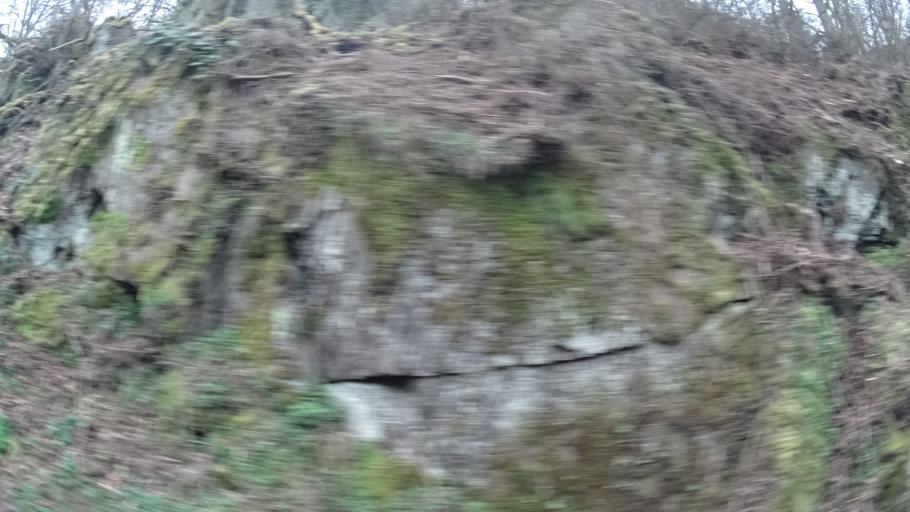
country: DE
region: Rheinland-Pfalz
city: Langenthal
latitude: 49.8481
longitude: 7.5753
